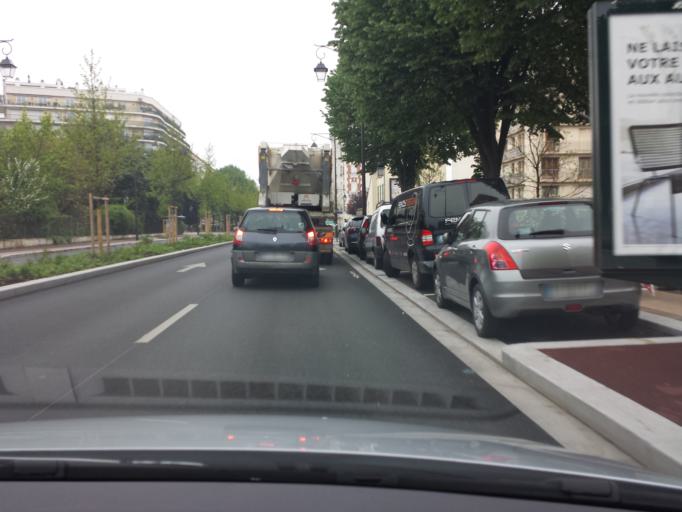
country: FR
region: Ile-de-France
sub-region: Departement des Hauts-de-Seine
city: Bourg-la-Reine
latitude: 48.7736
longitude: 2.3131
